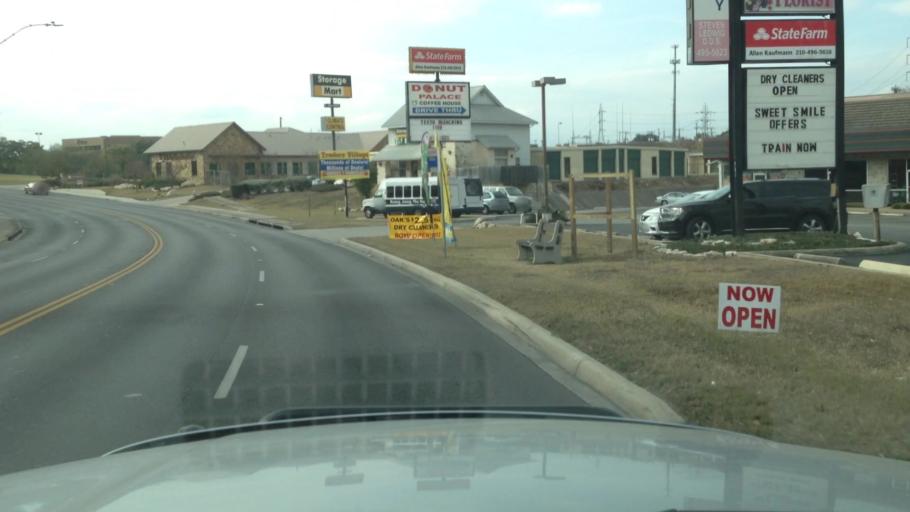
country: US
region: Texas
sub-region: Bexar County
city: Hollywood Park
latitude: 29.5921
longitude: -98.4675
